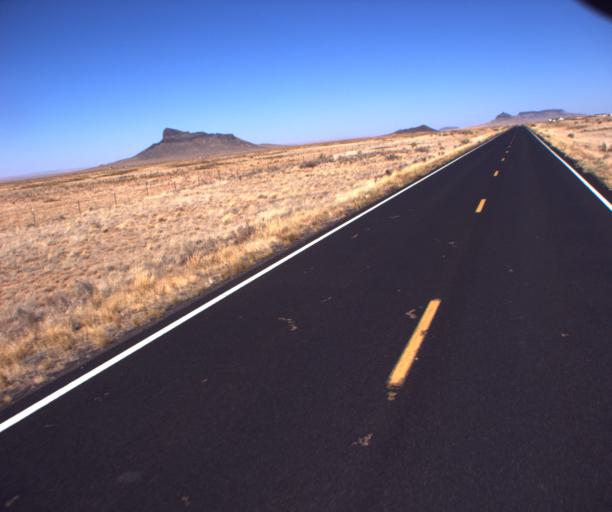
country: US
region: Arizona
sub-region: Navajo County
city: Dilkon
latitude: 35.4384
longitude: -110.4247
